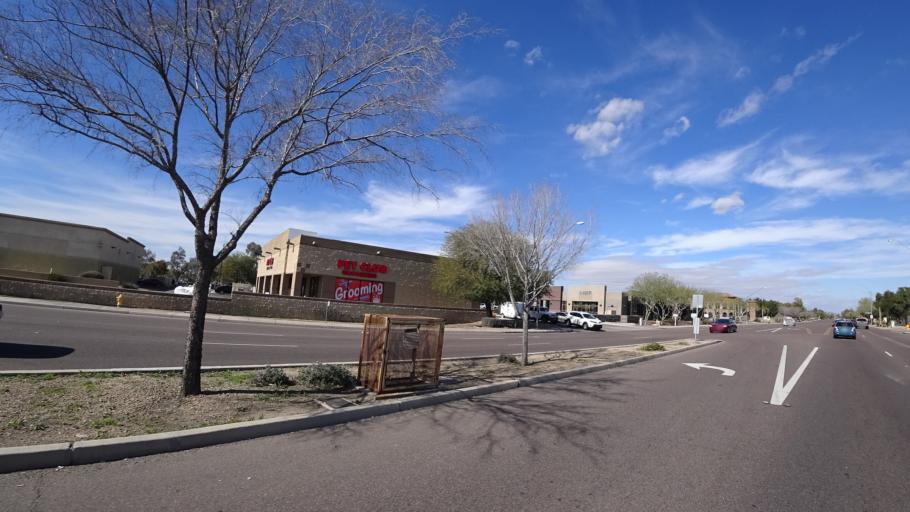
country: US
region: Arizona
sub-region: Maricopa County
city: Peoria
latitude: 33.6392
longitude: -112.2029
